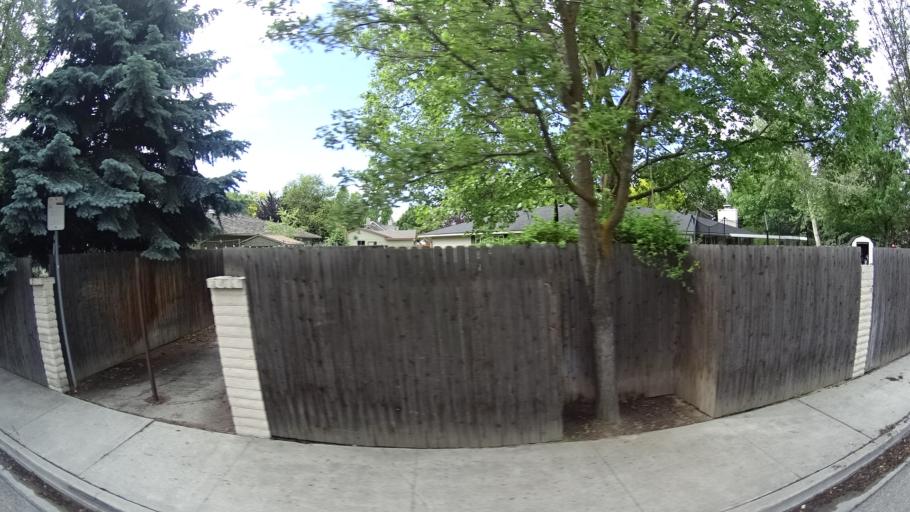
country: US
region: Idaho
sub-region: Ada County
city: Boise
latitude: 43.5789
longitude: -116.1873
